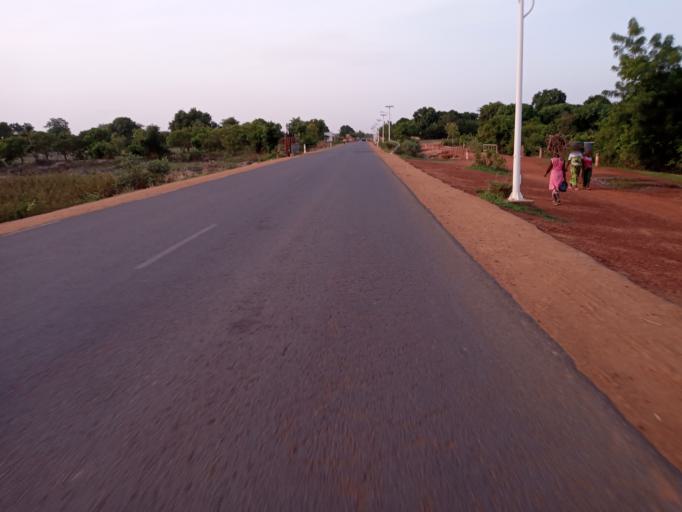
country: ML
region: Bamako
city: Bamako
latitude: 12.3034
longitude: -8.1570
